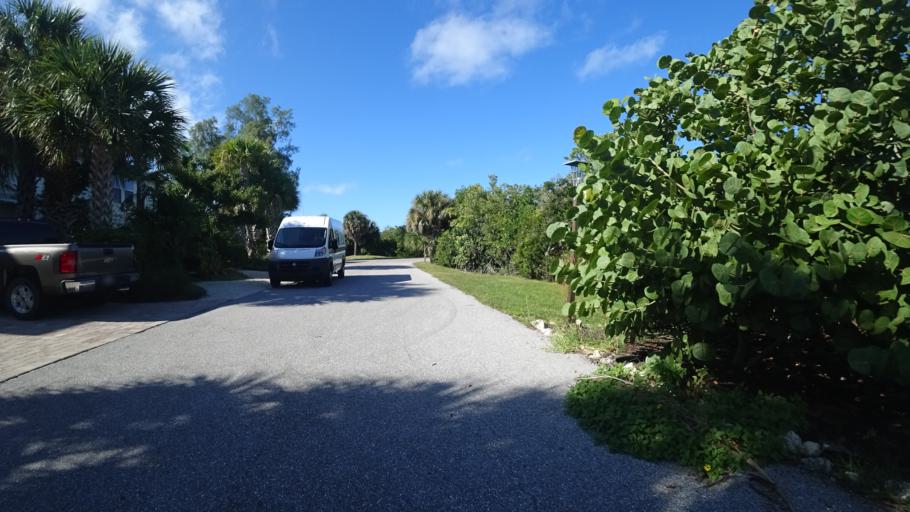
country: US
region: Florida
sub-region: Manatee County
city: Anna Maria
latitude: 27.5225
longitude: -82.7247
